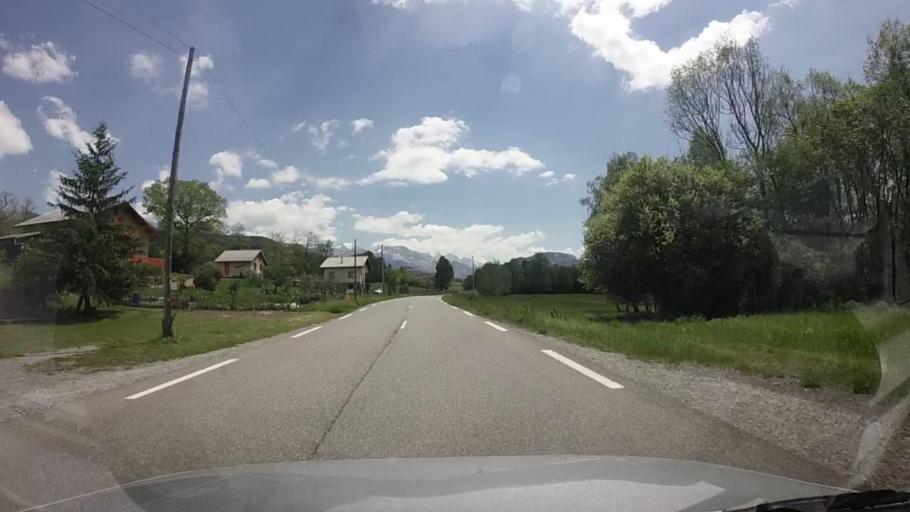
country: FR
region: Provence-Alpes-Cote d'Azur
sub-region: Departement des Alpes-de-Haute-Provence
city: Seyne-les-Alpes
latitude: 44.3661
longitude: 6.3208
